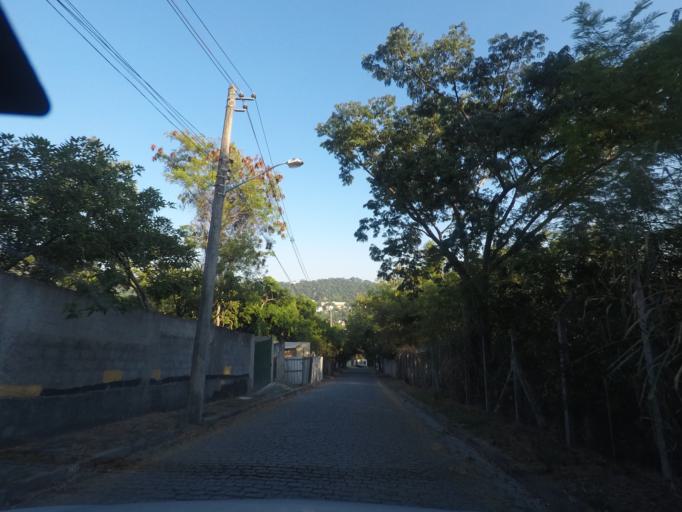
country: BR
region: Rio de Janeiro
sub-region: Rio De Janeiro
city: Rio de Janeiro
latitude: -22.9438
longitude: -43.1894
